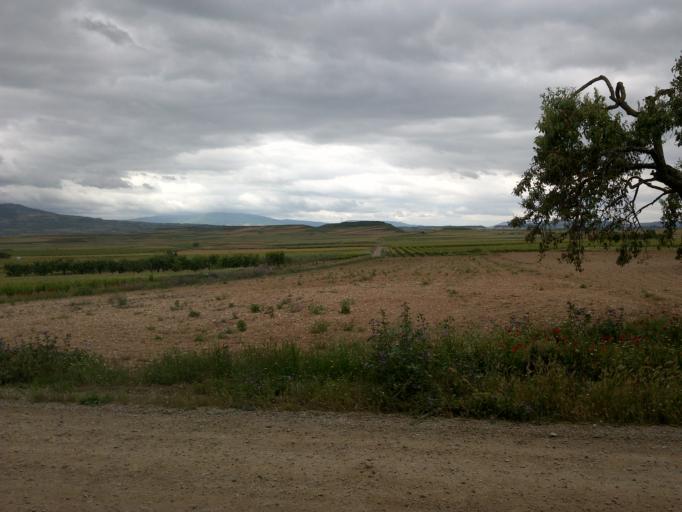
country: ES
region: La Rioja
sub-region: Provincia de La Rioja
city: Murillo de Rio Leza
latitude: 42.3984
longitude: -2.3382
